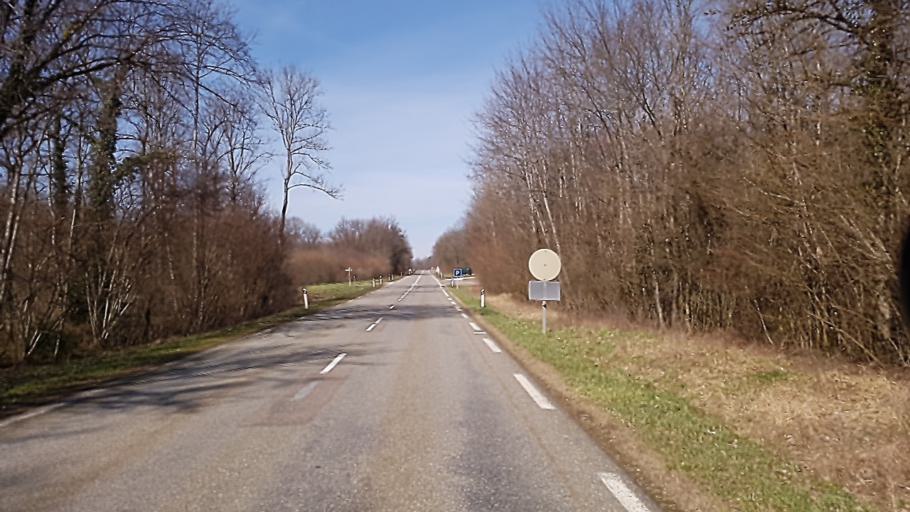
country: FR
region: Franche-Comte
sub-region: Departement du Jura
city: Poligny
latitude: 46.8152
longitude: 5.7795
